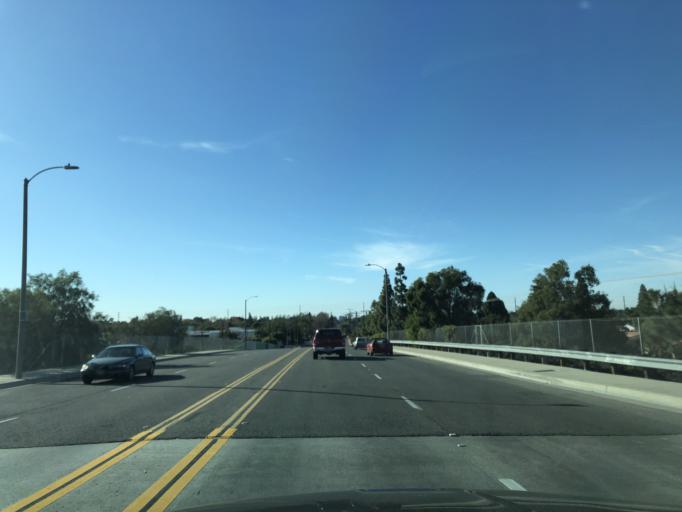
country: US
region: California
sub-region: Orange County
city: Orange
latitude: 33.7733
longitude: -117.8316
